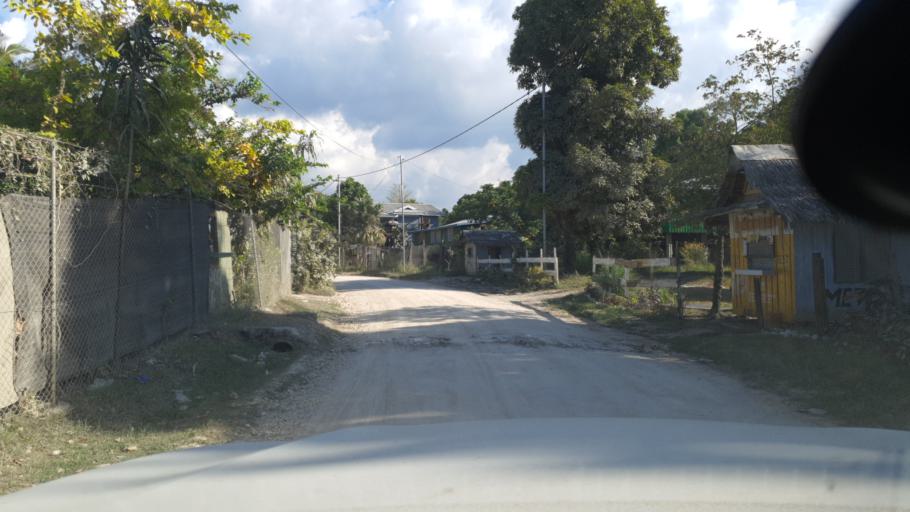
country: SB
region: Guadalcanal
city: Honiara
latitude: -9.4504
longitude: 159.9938
